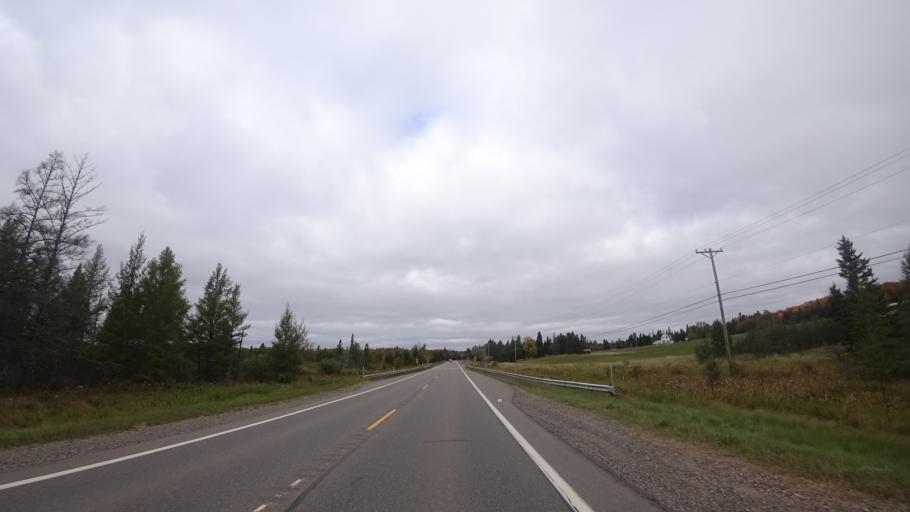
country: US
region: Michigan
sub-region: Iron County
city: Crystal Falls
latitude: 46.1194
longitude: -88.0882
